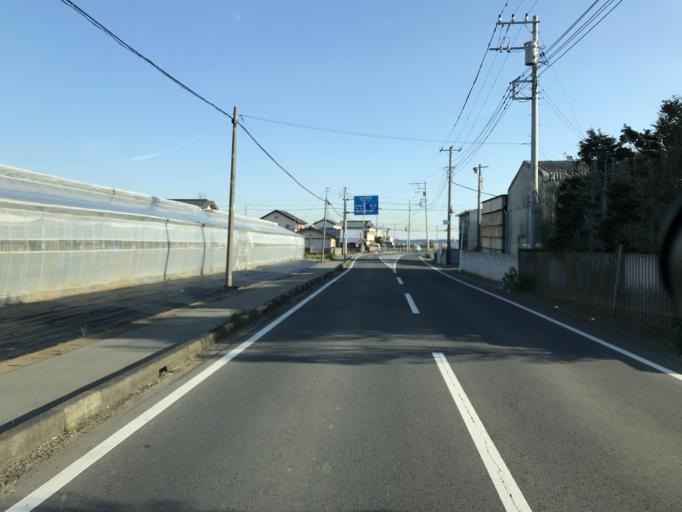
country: JP
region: Chiba
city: Asahi
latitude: 35.7111
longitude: 140.6889
